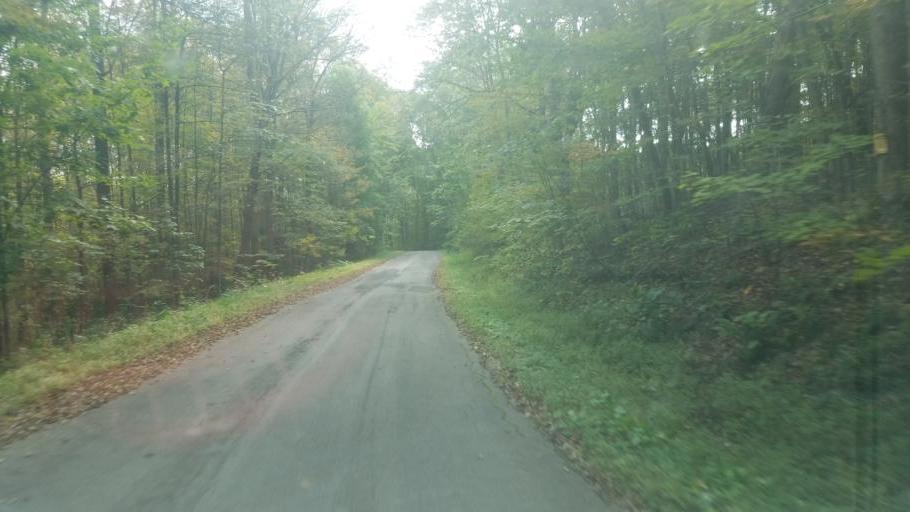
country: US
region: New York
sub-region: Allegany County
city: Cuba
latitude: 42.2270
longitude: -78.3492
